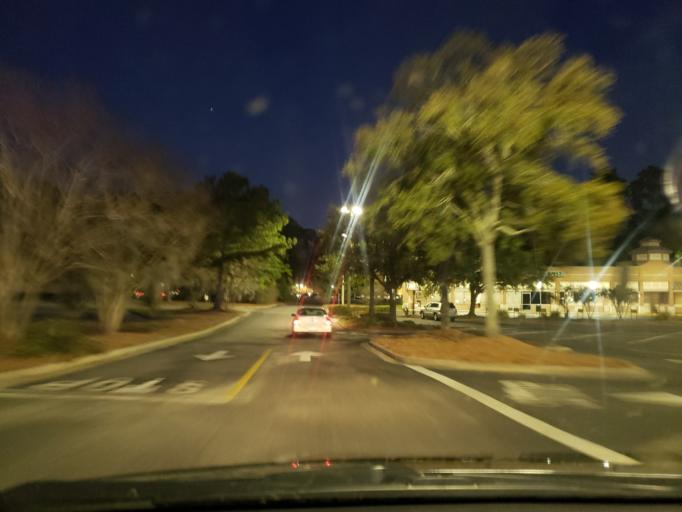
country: US
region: Georgia
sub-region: Chatham County
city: Georgetown
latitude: 31.9805
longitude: -81.1675
